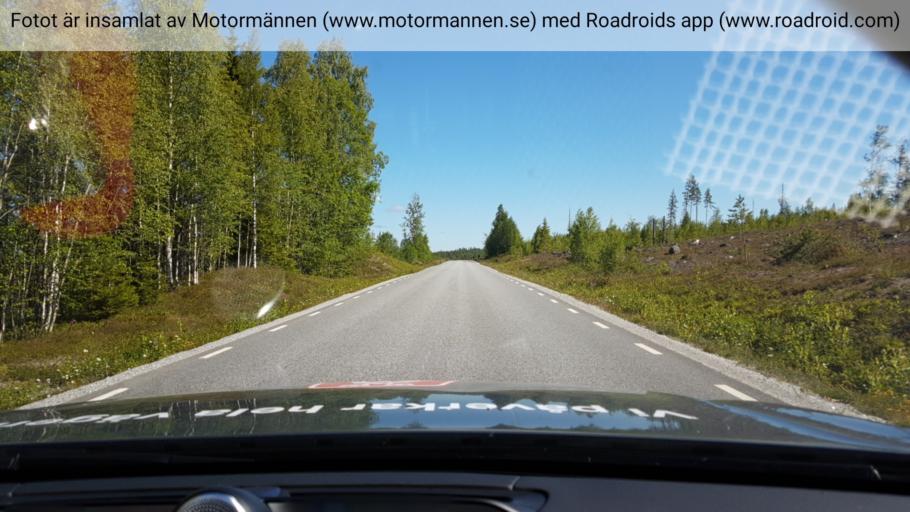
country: SE
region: Jaemtland
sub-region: Braecke Kommun
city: Braecke
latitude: 63.0917
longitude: 15.4357
